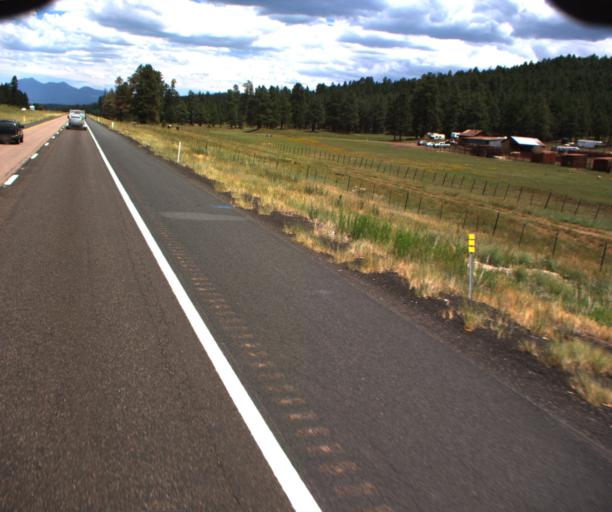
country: US
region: Arizona
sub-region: Coconino County
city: Mountainaire
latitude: 35.0090
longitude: -111.6852
